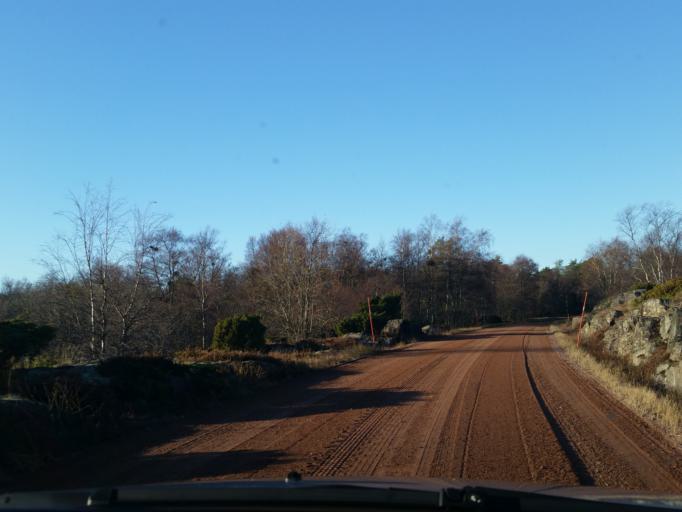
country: AX
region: Alands skaergard
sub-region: Braendoe
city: Braendoe
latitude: 60.4252
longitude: 20.9647
